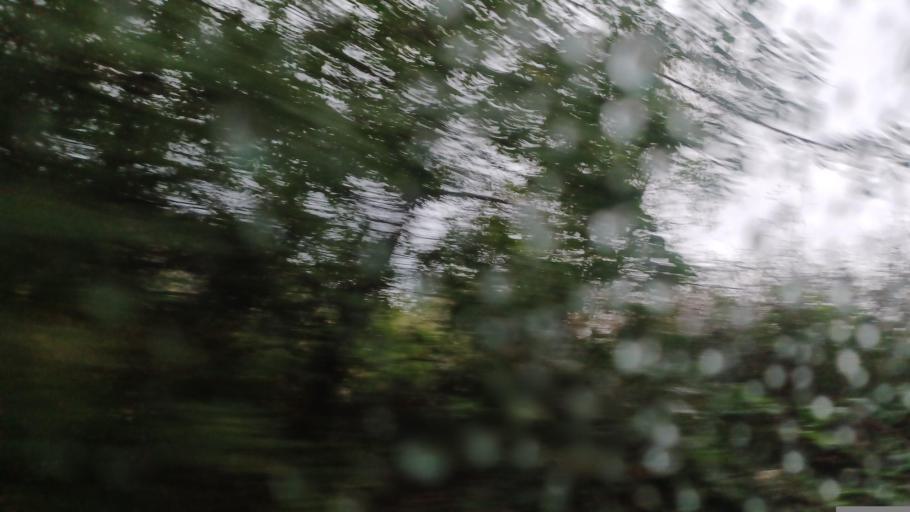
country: CY
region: Pafos
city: Mesogi
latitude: 34.8730
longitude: 32.5506
